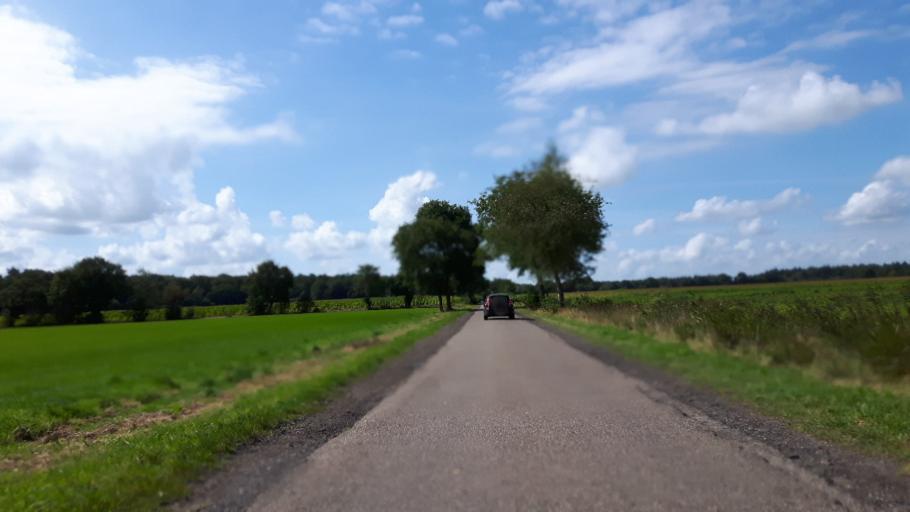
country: NL
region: Groningen
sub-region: Gemeente Leek
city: Leek
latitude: 53.0863
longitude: 6.3032
